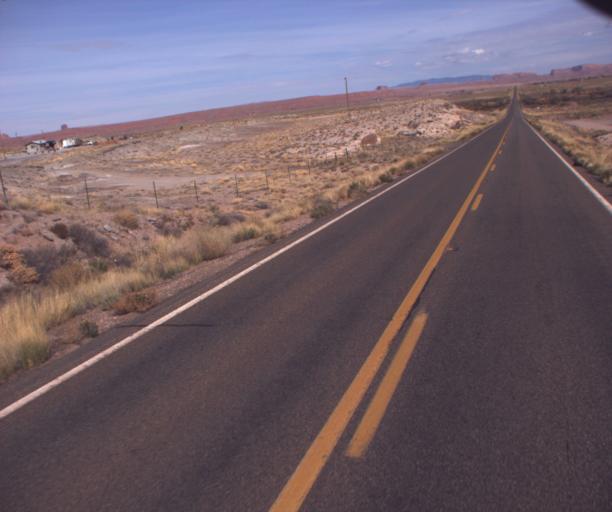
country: US
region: Arizona
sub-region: Apache County
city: Many Farms
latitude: 36.4896
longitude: -109.4978
